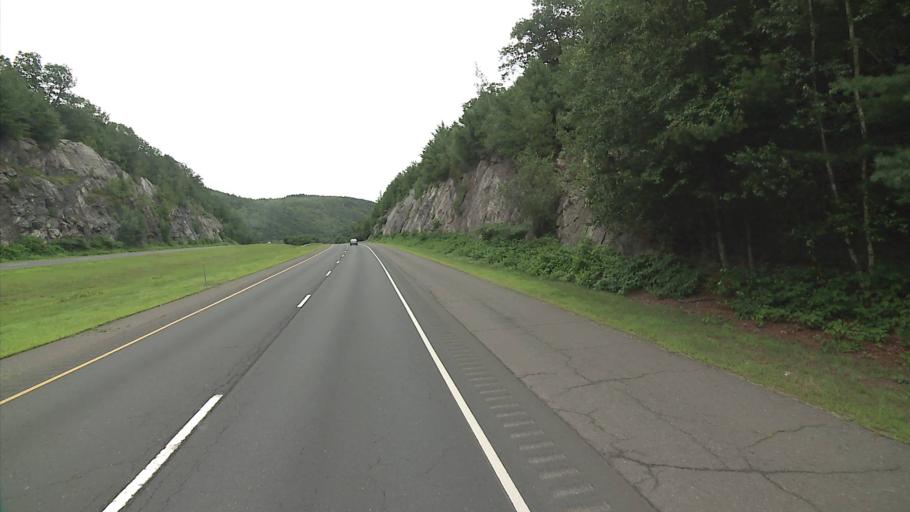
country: US
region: Connecticut
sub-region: New Haven County
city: Seymour
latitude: 41.4409
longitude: -73.0666
